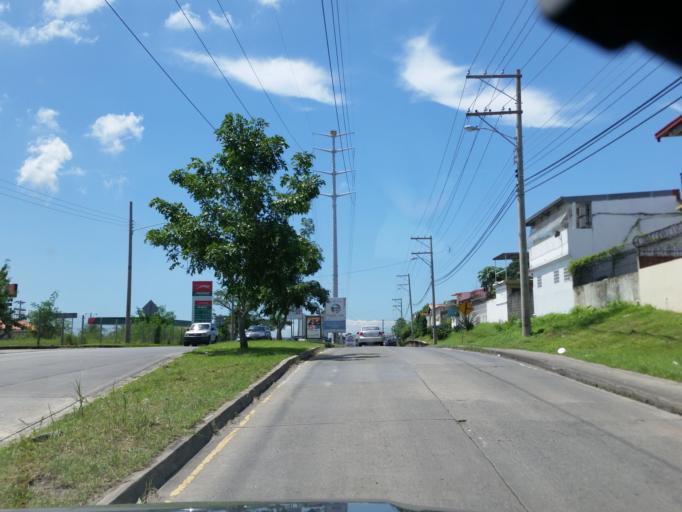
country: PA
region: Panama
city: San Miguelito
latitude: 9.0538
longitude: -79.4612
